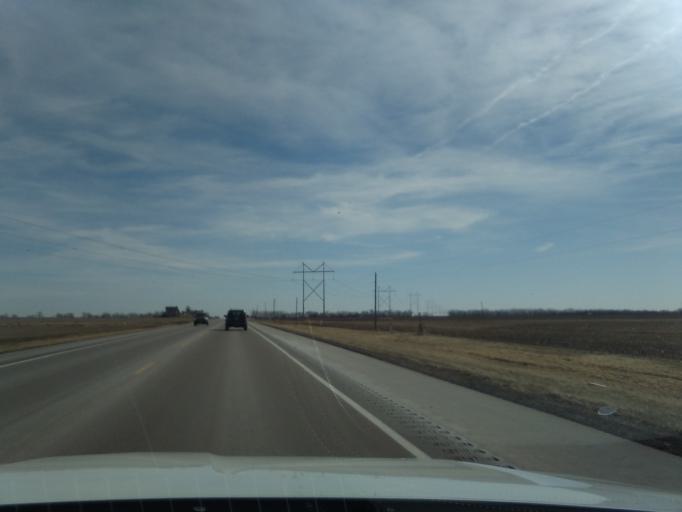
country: US
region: Nebraska
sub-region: Saline County
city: Friend
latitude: 40.6547
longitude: -97.2581
